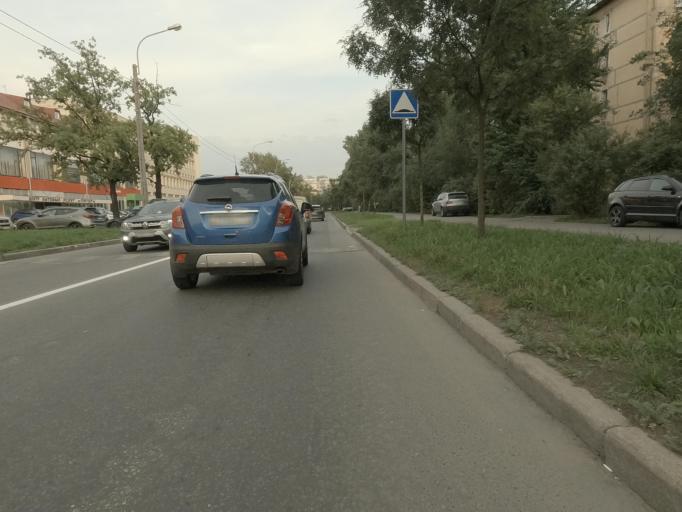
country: RU
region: St.-Petersburg
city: Dachnoye
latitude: 59.8552
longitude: 30.2637
